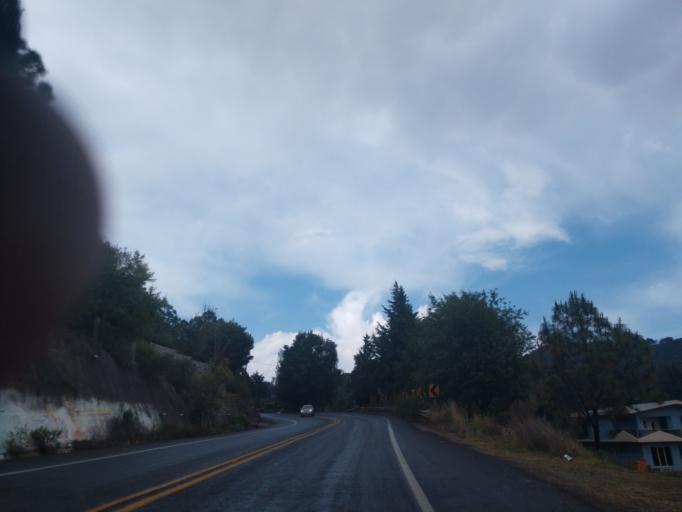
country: MX
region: Jalisco
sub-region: Mazamitla
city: Mazamitla
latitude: 19.9426
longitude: -103.0640
